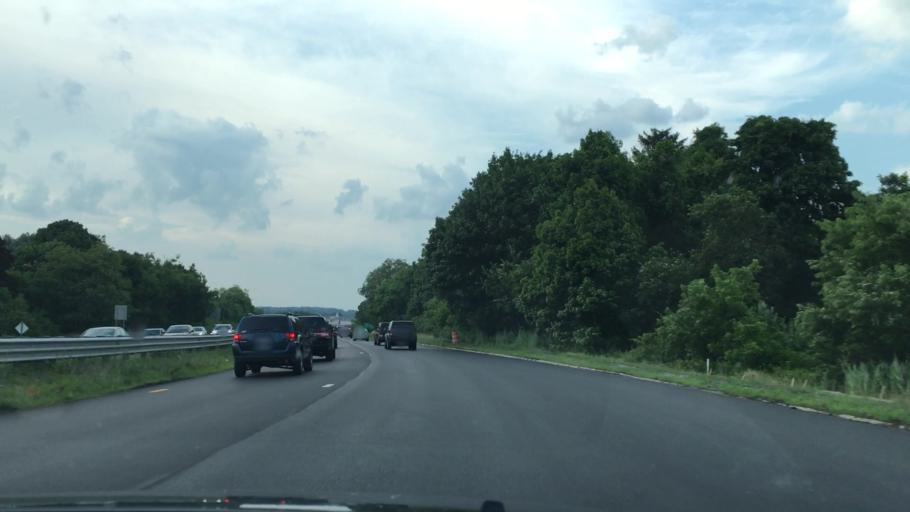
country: US
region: Massachusetts
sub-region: Essex County
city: Peabody
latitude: 42.5426
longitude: -70.9358
